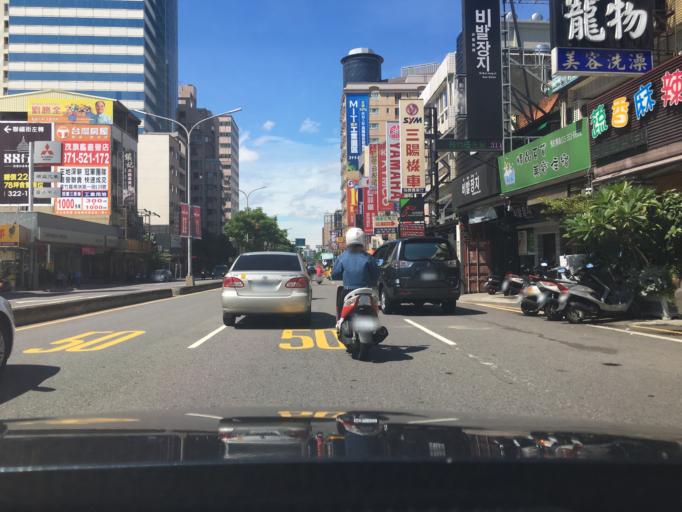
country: TW
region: Taiwan
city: Taoyuan City
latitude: 25.0508
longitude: 121.2900
